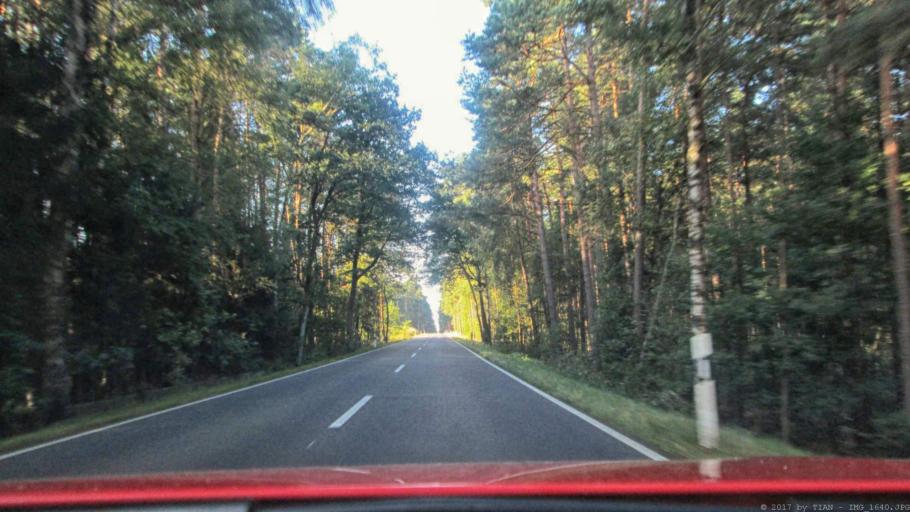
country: DE
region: Lower Saxony
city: Bergfeld
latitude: 52.6118
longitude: 10.8085
